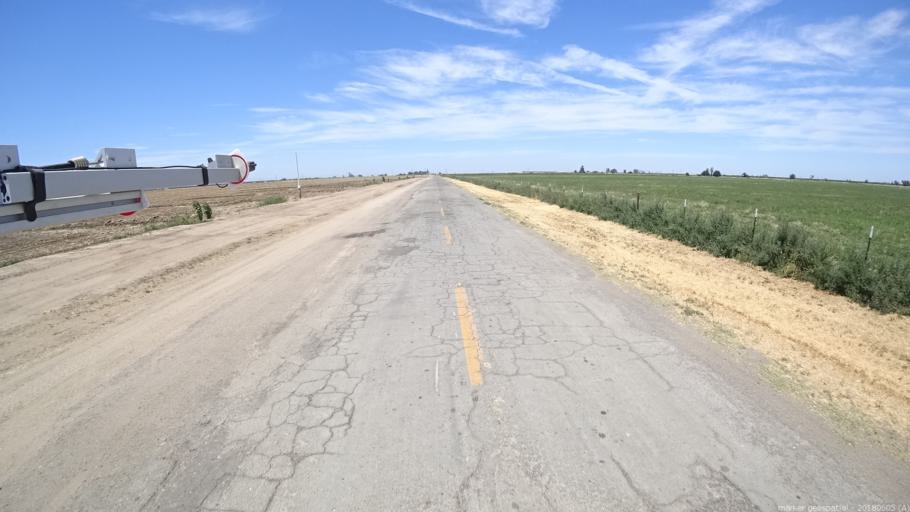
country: US
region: California
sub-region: Madera County
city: Chowchilla
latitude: 37.0906
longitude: -120.3364
